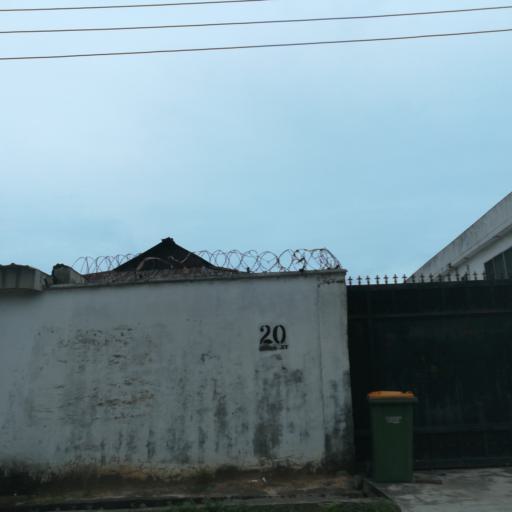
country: NG
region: Lagos
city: Makoko
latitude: 6.4987
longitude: 3.3803
